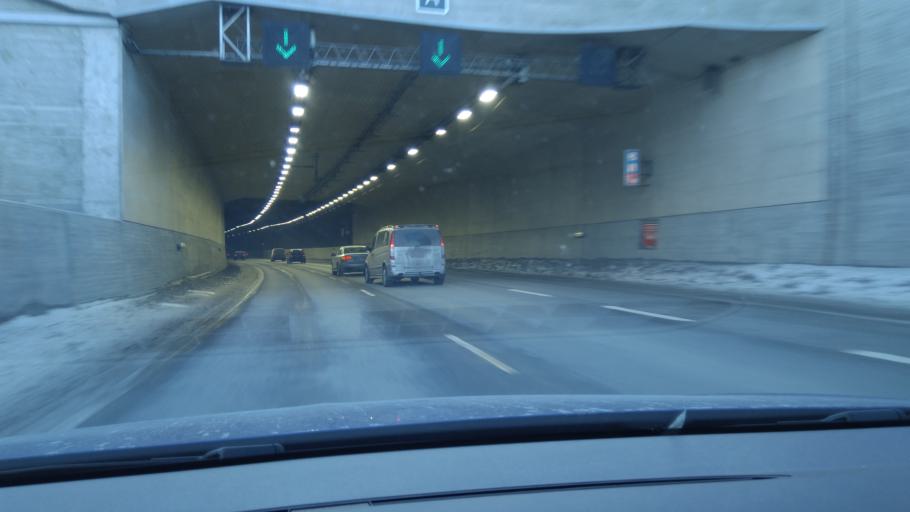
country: FI
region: Pirkanmaa
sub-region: Tampere
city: Tampere
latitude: 61.5015
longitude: 23.7313
